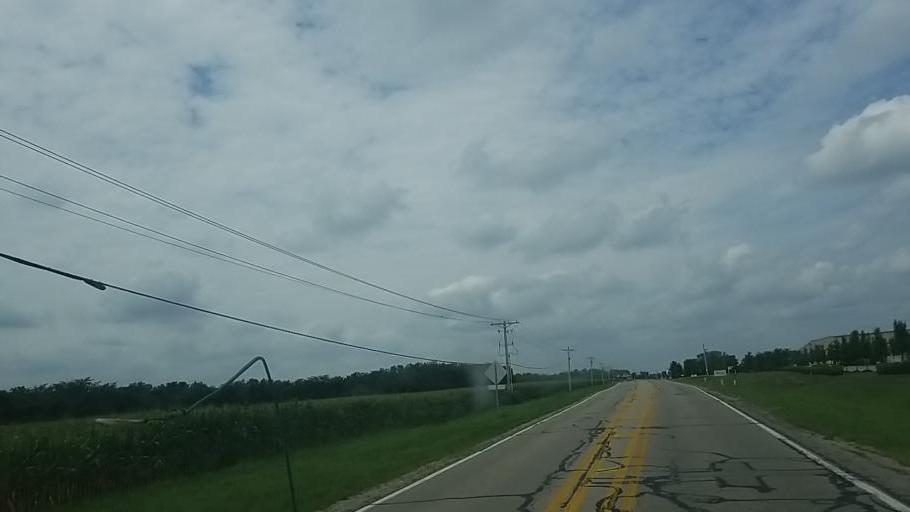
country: US
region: Ohio
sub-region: Franklin County
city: Groveport
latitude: 39.8293
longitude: -82.9025
